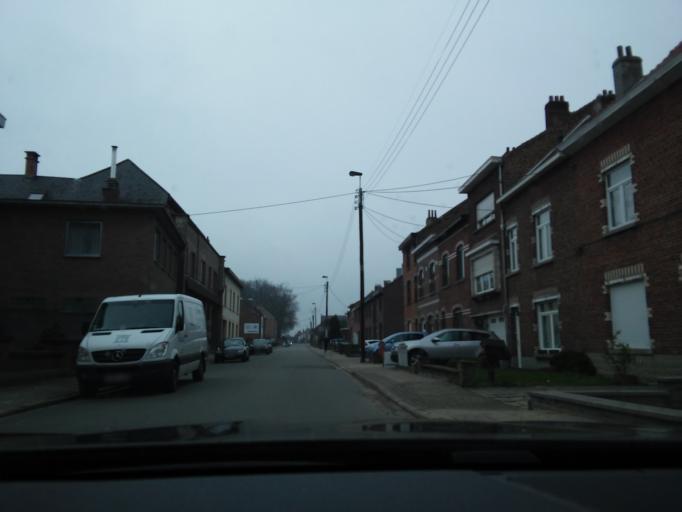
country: BE
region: Flanders
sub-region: Provincie Vlaams-Brabant
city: Asse
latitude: 50.8798
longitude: 4.2225
